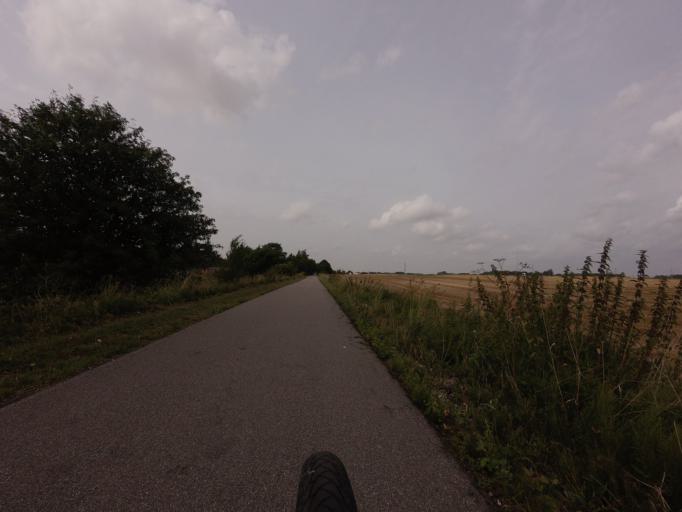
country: DK
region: Zealand
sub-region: Naestved Kommune
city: Naestved
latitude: 55.2524
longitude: 11.7213
